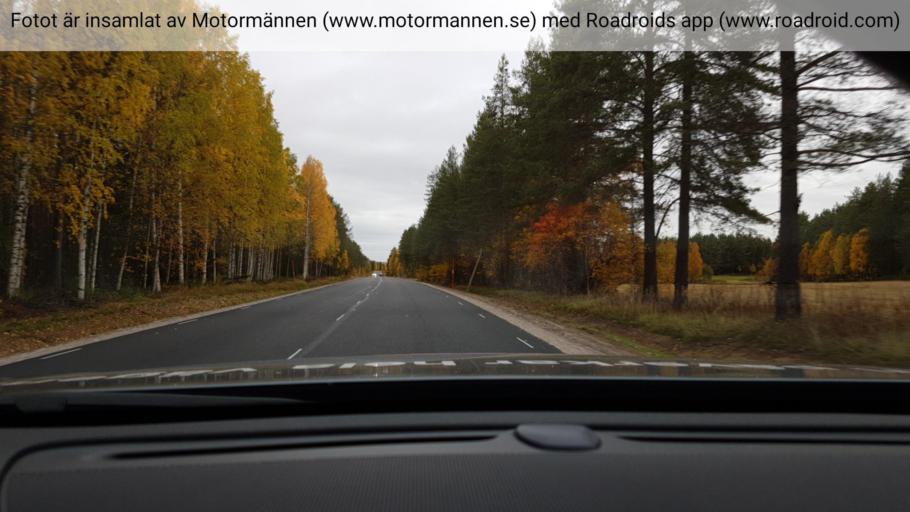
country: SE
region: Norrbotten
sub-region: Overkalix Kommun
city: OEverkalix
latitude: 66.4349
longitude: 22.7937
